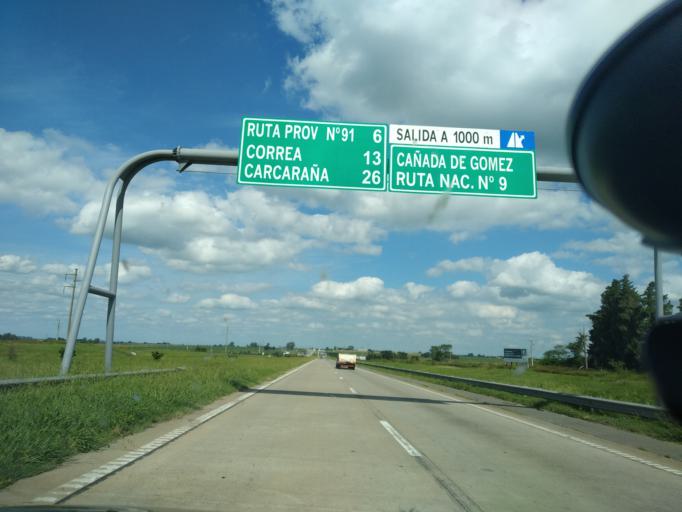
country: AR
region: Santa Fe
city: Canada de Gomez
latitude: -32.8441
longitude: -61.4063
